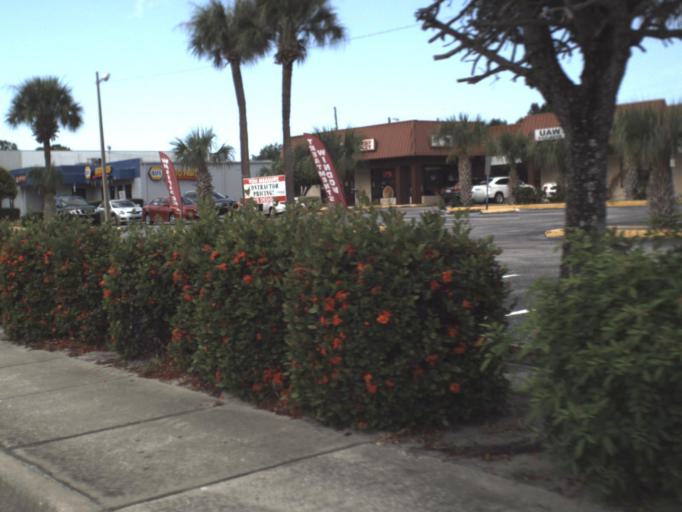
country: US
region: Florida
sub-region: Pinellas County
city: Seminole
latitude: 27.8592
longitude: -82.7872
